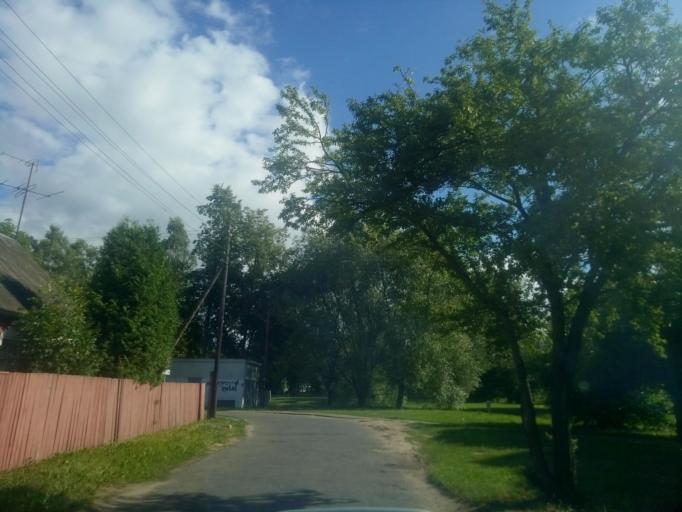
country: BY
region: Minsk
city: Novoye Medvezhino
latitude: 53.8885
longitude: 27.5066
